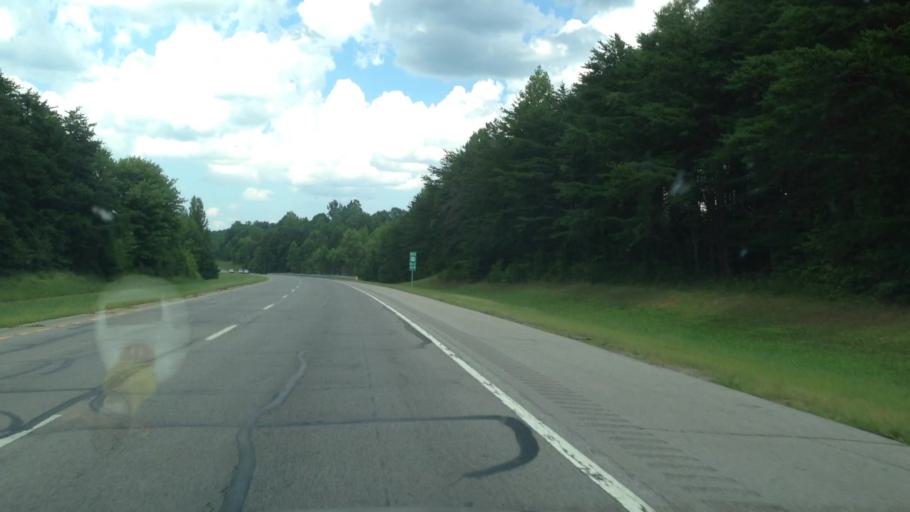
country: US
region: Virginia
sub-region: City of Danville
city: Danville
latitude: 36.4767
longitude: -79.5043
